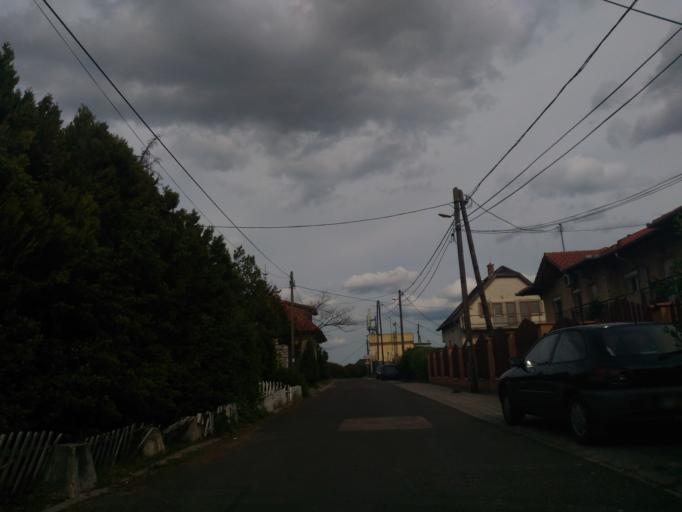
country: HU
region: Budapest
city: Budapest XXII. keruelet
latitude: 47.4278
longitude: 19.0286
